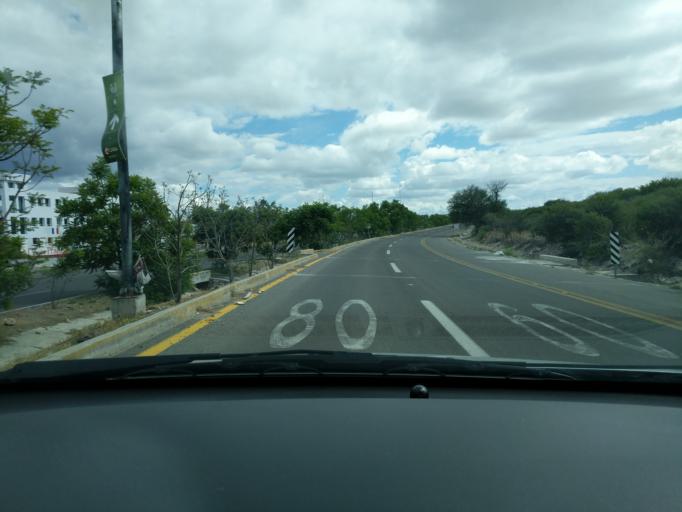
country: MX
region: Queretaro
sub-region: El Marques
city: La Pradera
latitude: 20.6673
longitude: -100.3122
